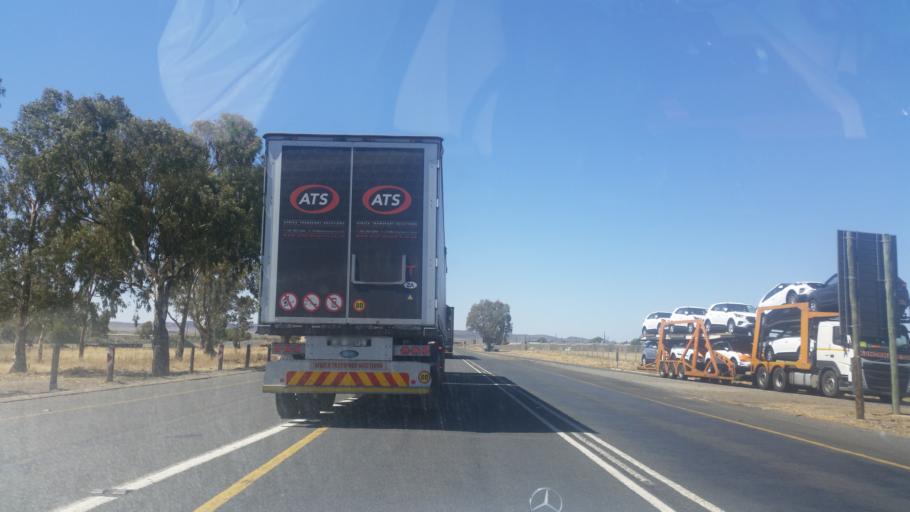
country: ZA
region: Northern Cape
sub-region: Pixley ka Seme District Municipality
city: Colesberg
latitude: -30.7083
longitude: 25.1083
